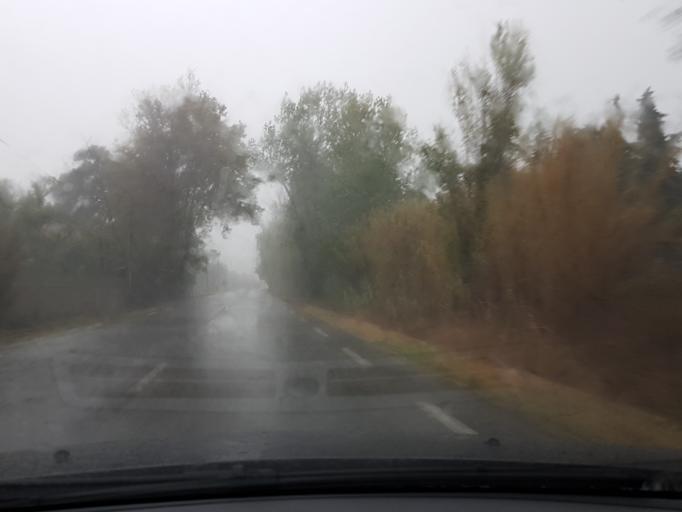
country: FR
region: Provence-Alpes-Cote d'Azur
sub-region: Departement du Vaucluse
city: Pernes-les-Fontaines
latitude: 44.0120
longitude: 5.0269
